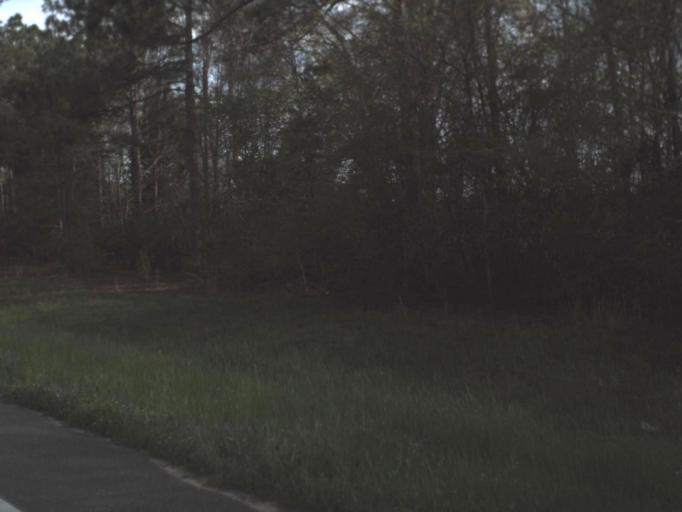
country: US
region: Florida
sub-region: Holmes County
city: Bonifay
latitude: 30.7854
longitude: -85.6531
